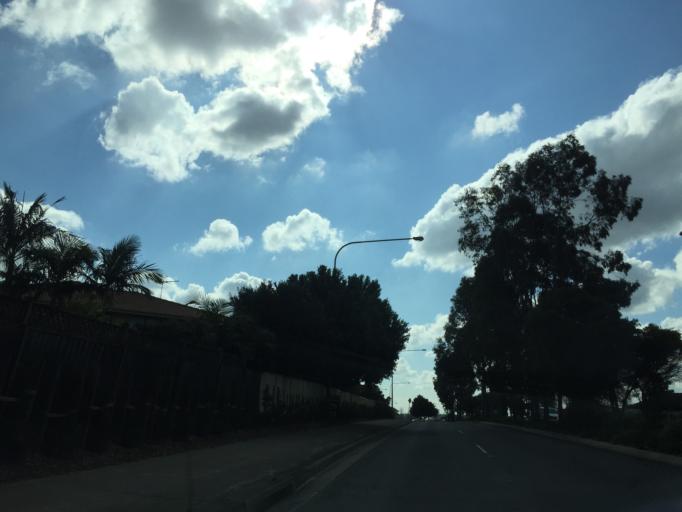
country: AU
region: New South Wales
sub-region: Blacktown
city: Quakers Hill
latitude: -33.7148
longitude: 150.8929
